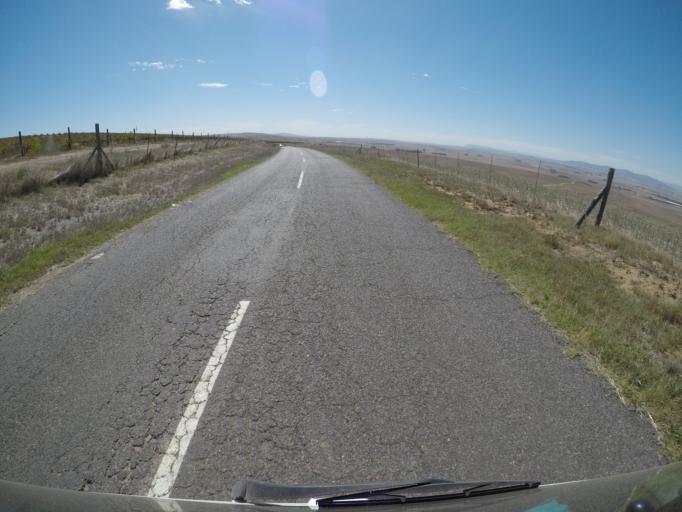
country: ZA
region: Western Cape
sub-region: City of Cape Town
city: Sunset Beach
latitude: -33.7151
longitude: 18.5826
